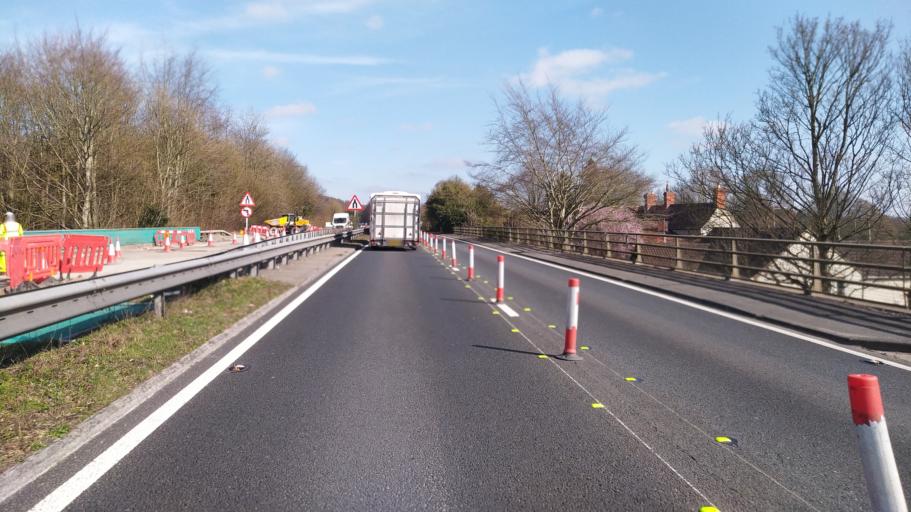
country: GB
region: England
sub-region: Wiltshire
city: Mere
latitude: 51.0947
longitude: -2.2623
